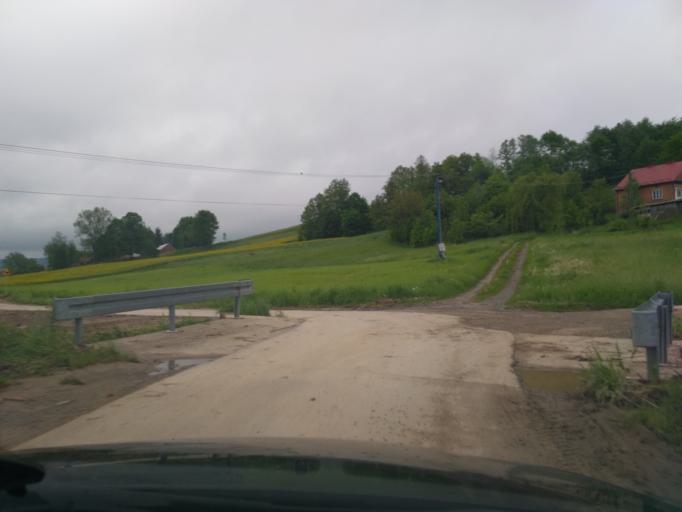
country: PL
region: Subcarpathian Voivodeship
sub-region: Powiat ropczycko-sedziszowski
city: Niedzwiada
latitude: 49.9740
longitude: 21.5389
